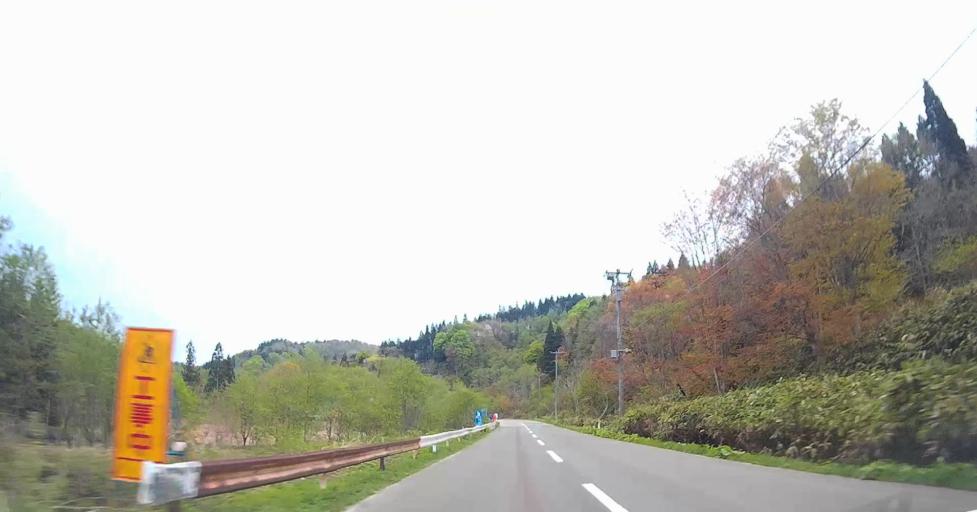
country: JP
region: Aomori
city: Goshogawara
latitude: 41.1200
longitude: 140.5235
